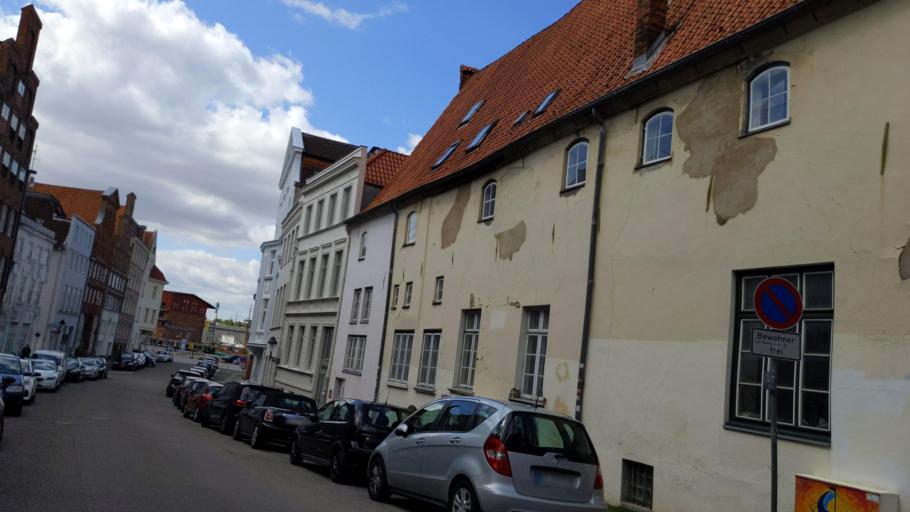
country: DE
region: Schleswig-Holstein
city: Luebeck
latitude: 53.8730
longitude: 10.6889
